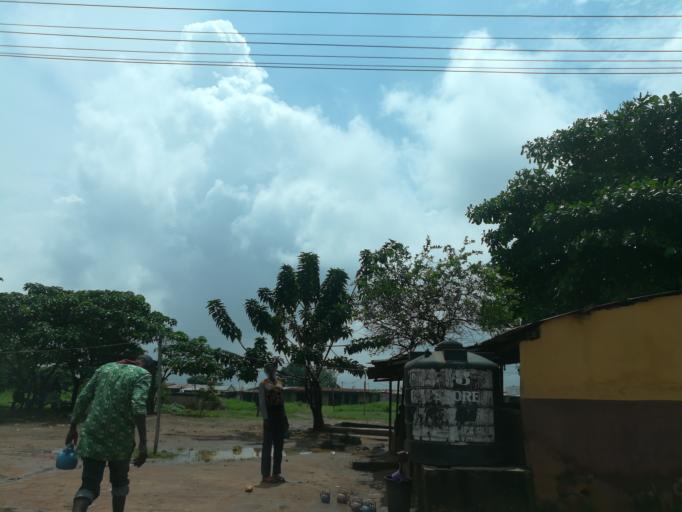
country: NG
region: Lagos
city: Ikorodu
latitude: 6.6779
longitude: 3.5121
